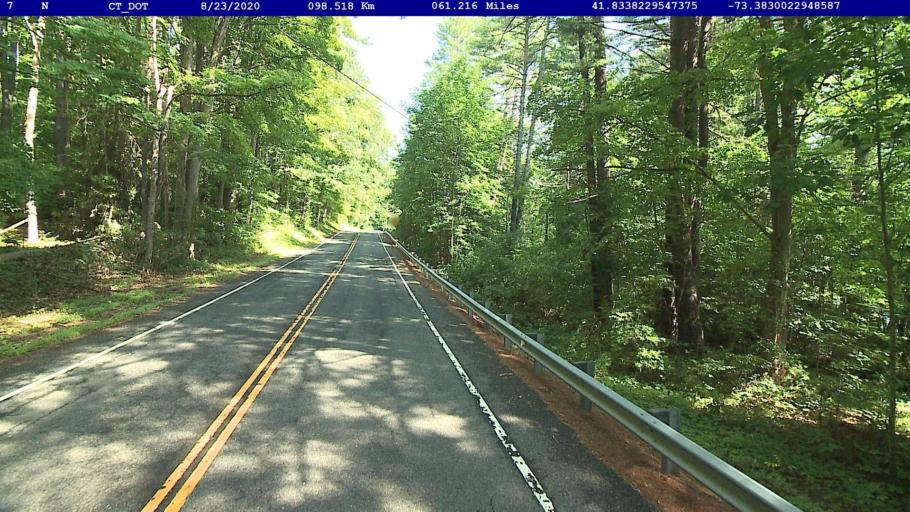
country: US
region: Connecticut
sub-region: Litchfield County
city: Kent
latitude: 41.8338
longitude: -73.3830
